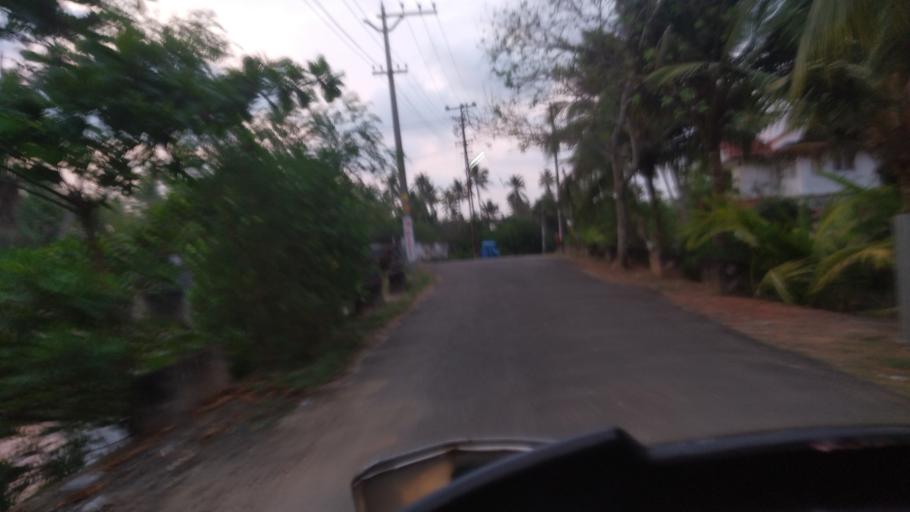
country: IN
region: Kerala
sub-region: Thrissur District
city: Kodungallur
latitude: 10.1458
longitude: 76.2101
